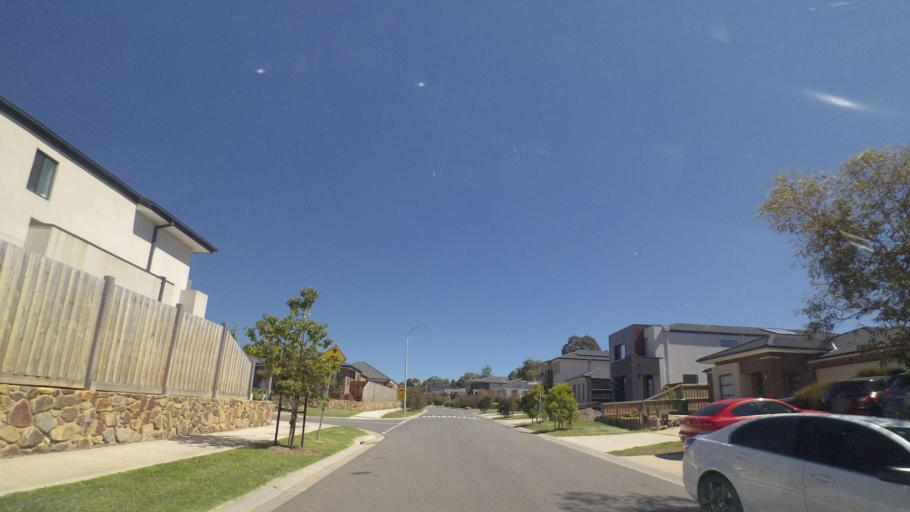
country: AU
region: Victoria
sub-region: Yarra Ranges
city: Chirnside Park
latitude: -37.7489
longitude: 145.3214
